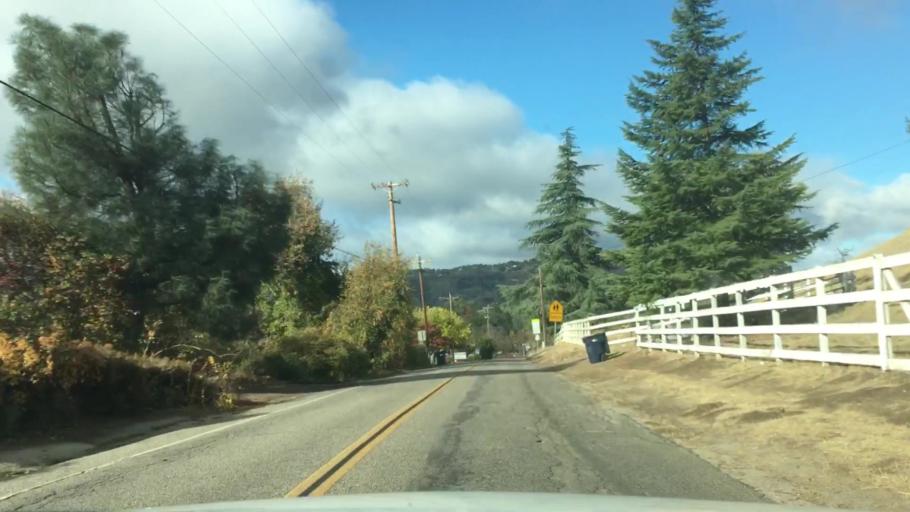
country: US
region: California
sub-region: San Luis Obispo County
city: Atascadero
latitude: 35.4589
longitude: -120.6668
